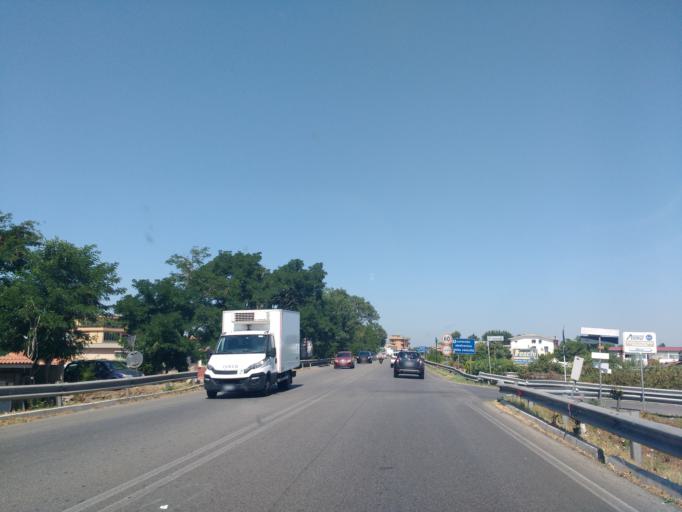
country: IT
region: Latium
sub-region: Citta metropolitana di Roma Capitale
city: Lido di Ostia
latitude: 41.7580
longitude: 12.2732
